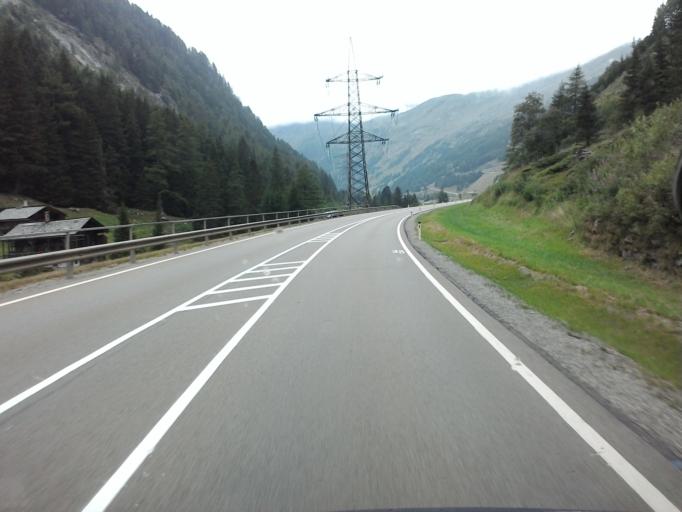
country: AT
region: Tyrol
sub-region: Politischer Bezirk Lienz
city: Matrei in Osttirol
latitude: 47.1044
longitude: 12.5067
